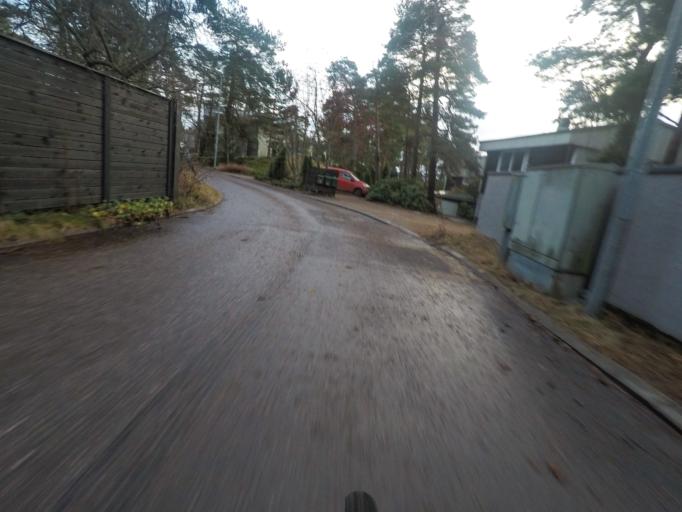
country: FI
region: Uusimaa
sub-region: Helsinki
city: Helsinki
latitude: 60.1596
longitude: 25.0640
